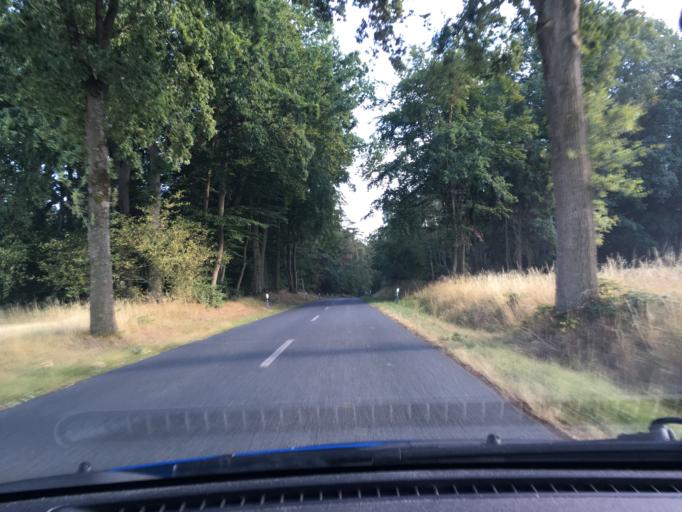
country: DE
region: Lower Saxony
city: Bleckede
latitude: 53.2538
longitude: 10.7095
